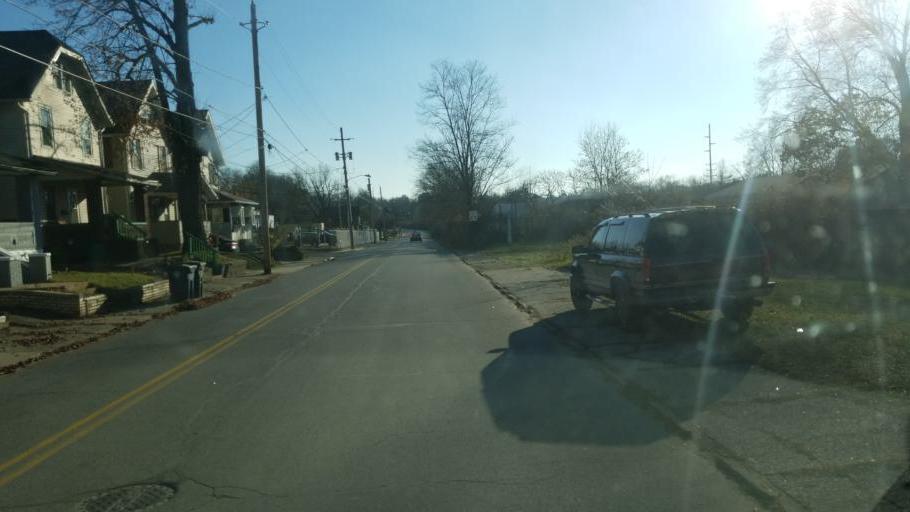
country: US
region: Ohio
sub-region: Summit County
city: Akron
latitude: 41.0800
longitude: -81.4821
